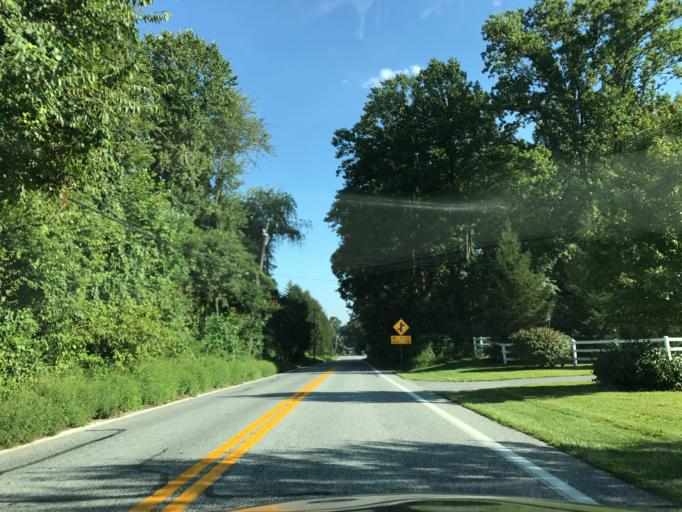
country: US
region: Maryland
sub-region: Harford County
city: Jarrettsville
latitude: 39.5954
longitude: -76.5703
